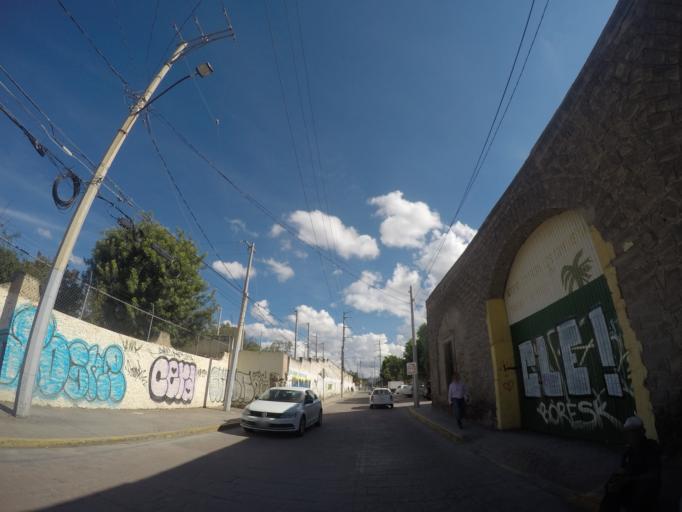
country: MX
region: San Luis Potosi
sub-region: San Luis Potosi
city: San Luis Potosi
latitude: 22.1548
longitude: -100.9679
